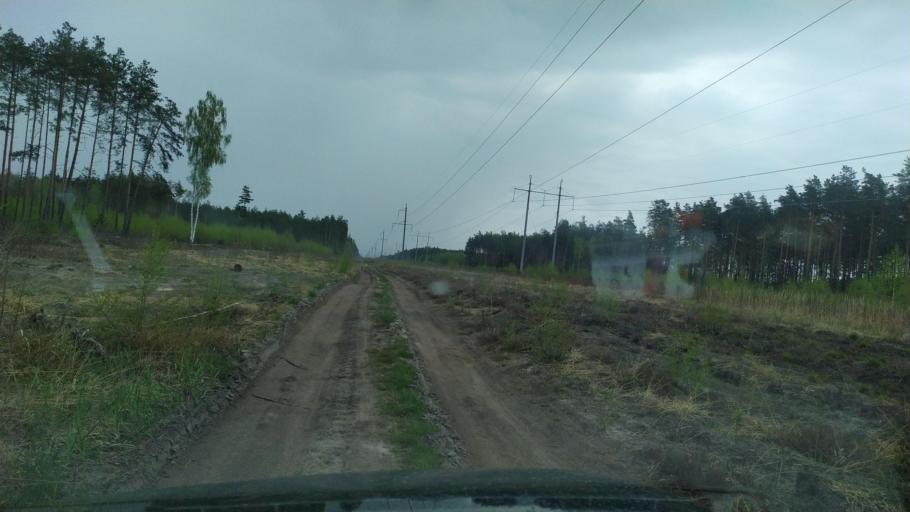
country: BY
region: Brest
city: Pruzhany
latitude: 52.3616
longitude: 24.5930
